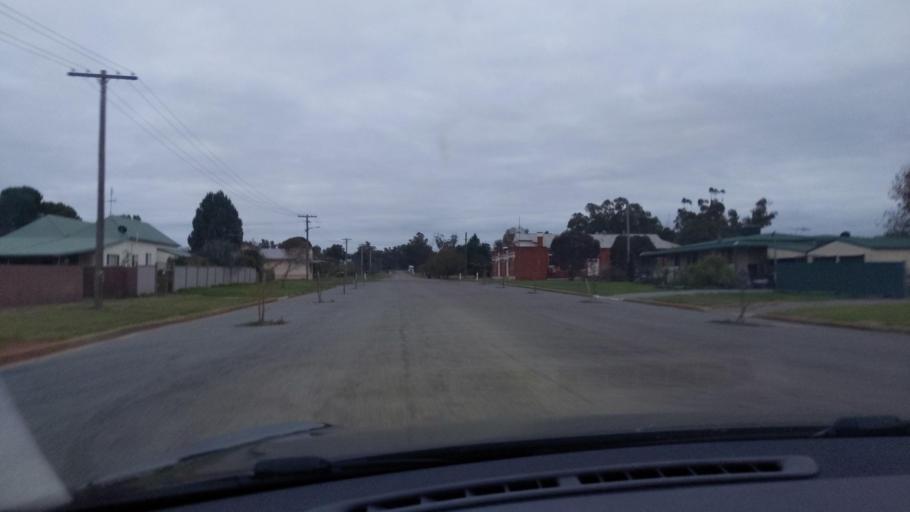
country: AU
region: New South Wales
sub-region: Narrandera
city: Narrandera
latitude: -34.7383
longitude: 146.7829
